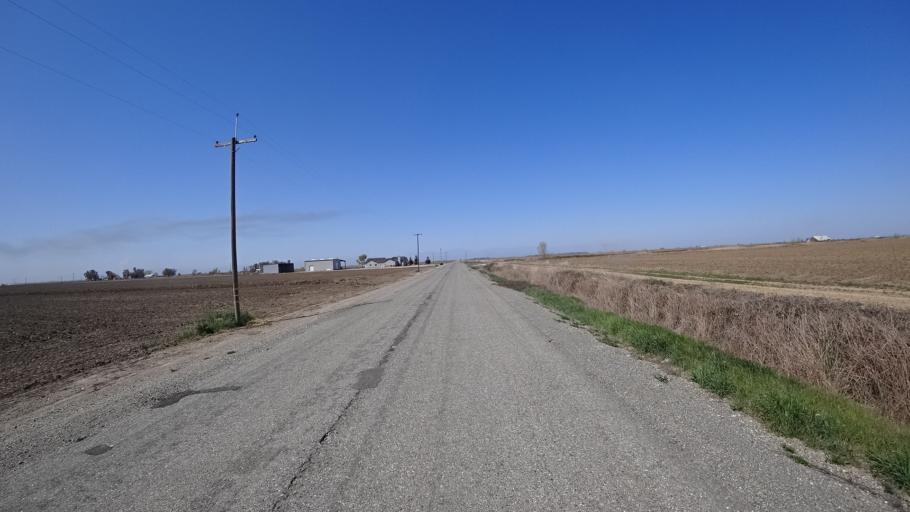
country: US
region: California
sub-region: Glenn County
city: Willows
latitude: 39.4285
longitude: -122.0428
